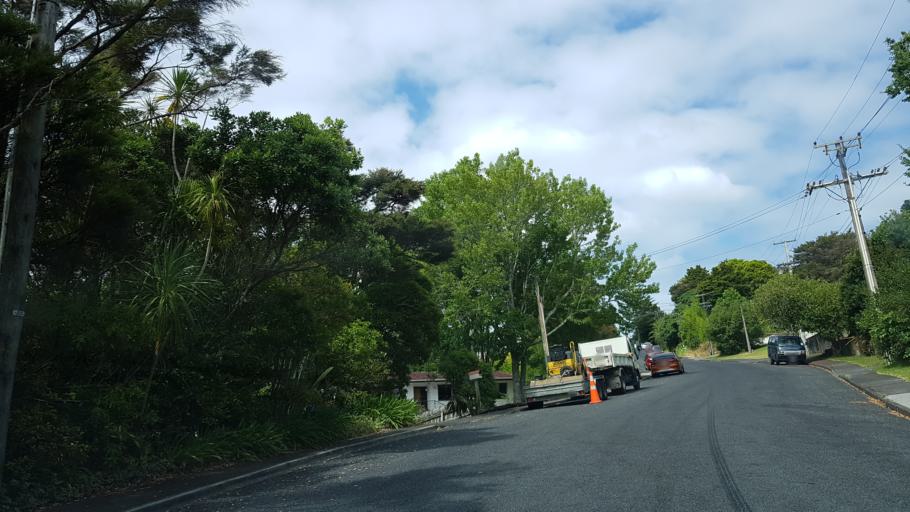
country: NZ
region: Auckland
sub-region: Auckland
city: North Shore
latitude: -36.7792
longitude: 174.7026
